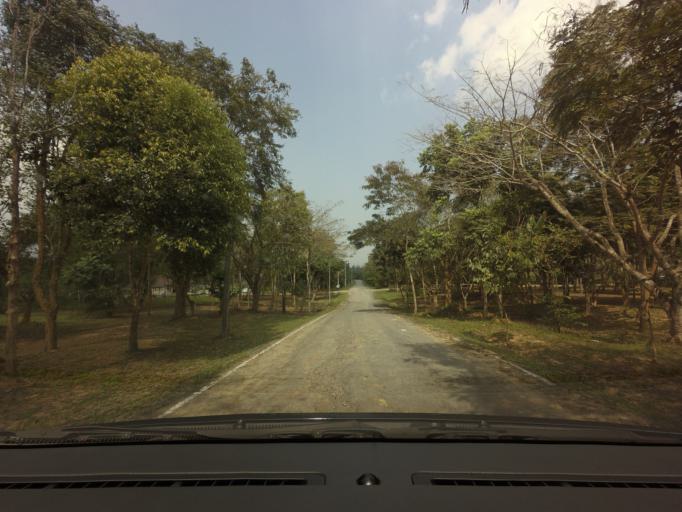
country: TH
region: Prachuap Khiri Khan
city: Kui Buri
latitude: 12.0522
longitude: 99.6245
